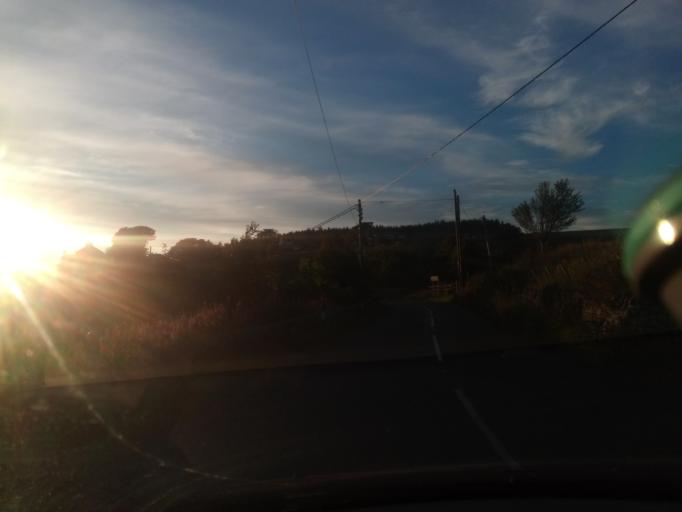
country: GB
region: England
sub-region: County Durham
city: Holwick
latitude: 54.7673
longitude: -2.2416
